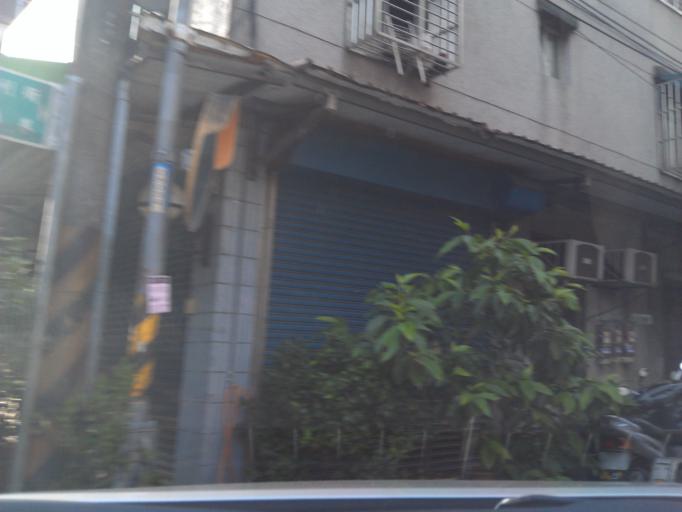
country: TW
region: Taipei
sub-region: Taipei
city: Banqiao
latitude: 24.9992
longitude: 121.4806
